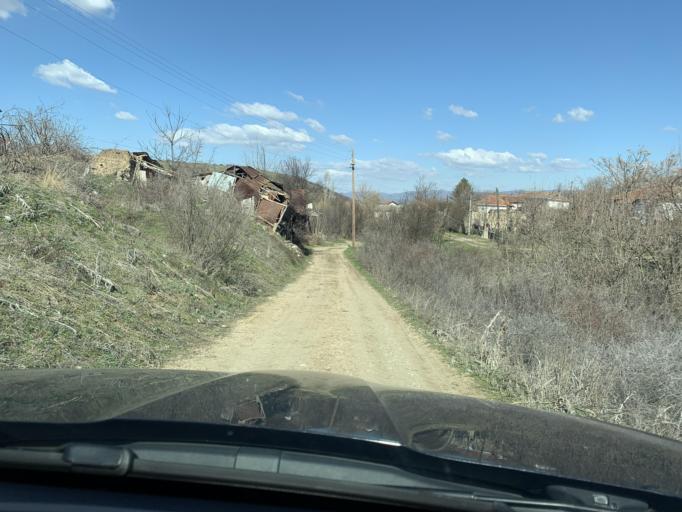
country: MK
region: Demir Kapija
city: Demir Kapija
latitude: 41.4173
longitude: 22.1663
